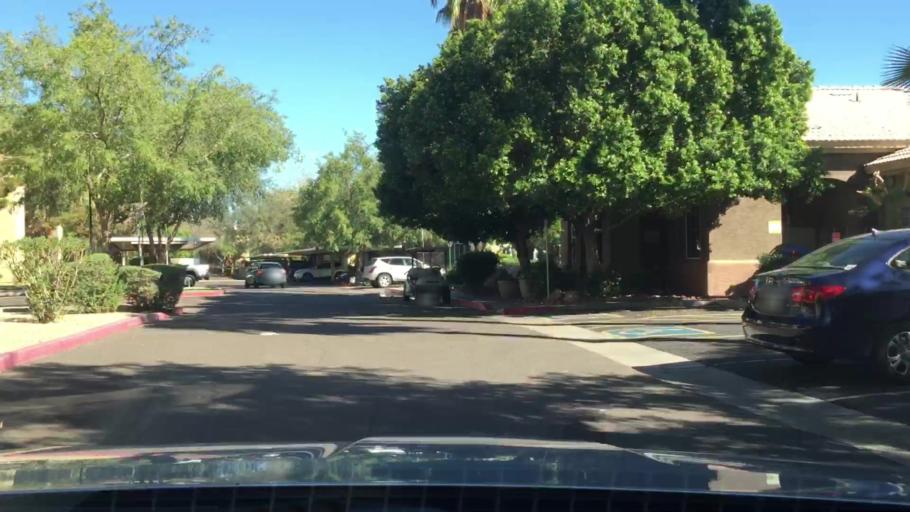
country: US
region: Arizona
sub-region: Maricopa County
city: Gilbert
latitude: 33.3773
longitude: -111.7458
